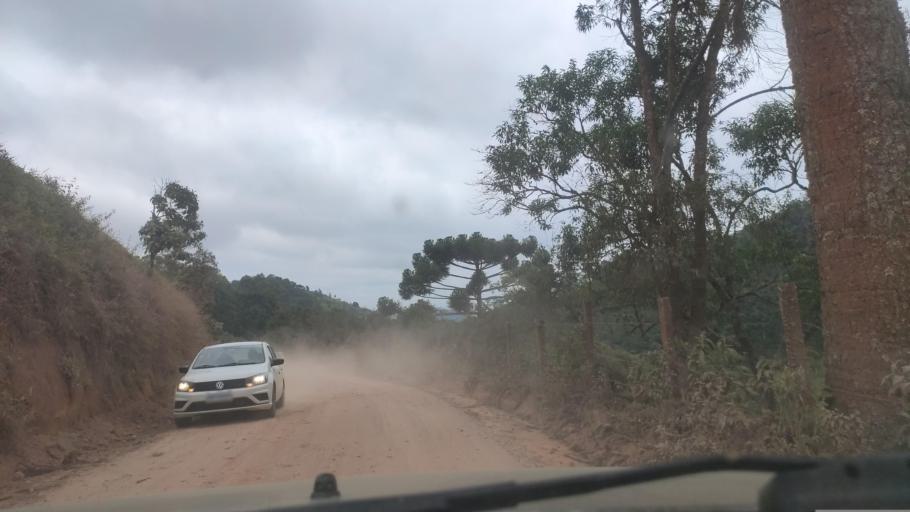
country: BR
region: Minas Gerais
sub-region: Paraisopolis
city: Paraisopolis
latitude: -22.6601
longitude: -45.8839
